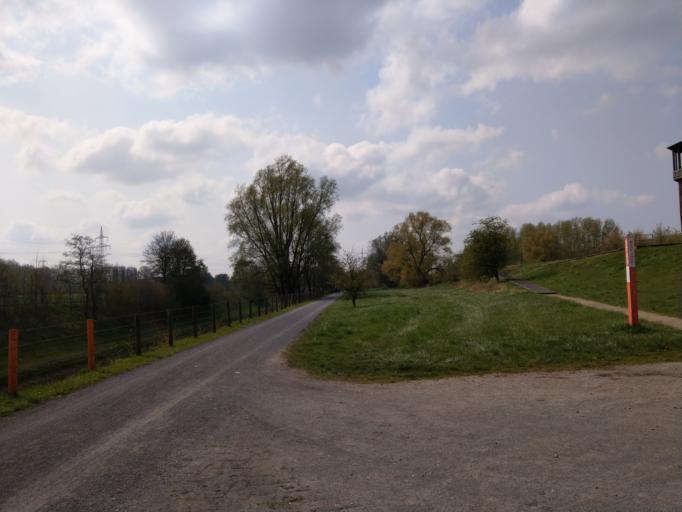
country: DE
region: North Rhine-Westphalia
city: Castrop-Rauxel
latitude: 51.5900
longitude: 7.2871
